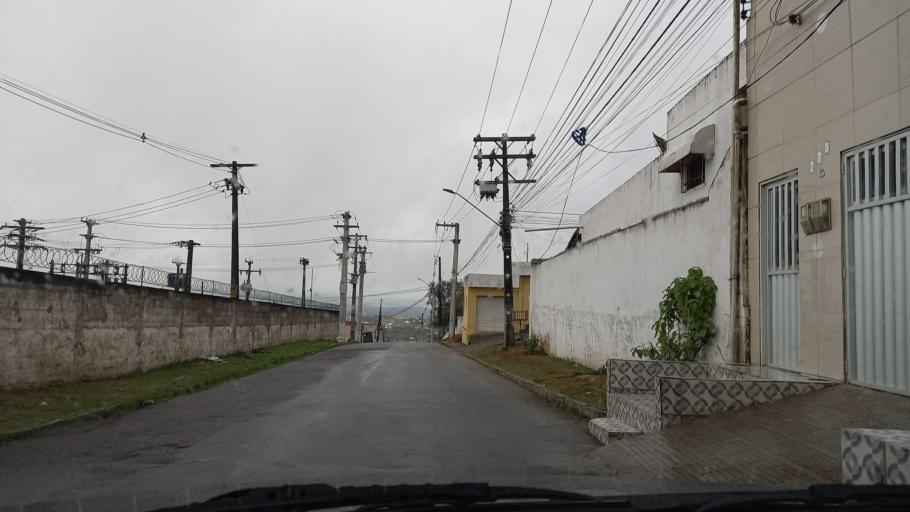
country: BR
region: Pernambuco
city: Garanhuns
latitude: -8.8842
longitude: -36.4947
